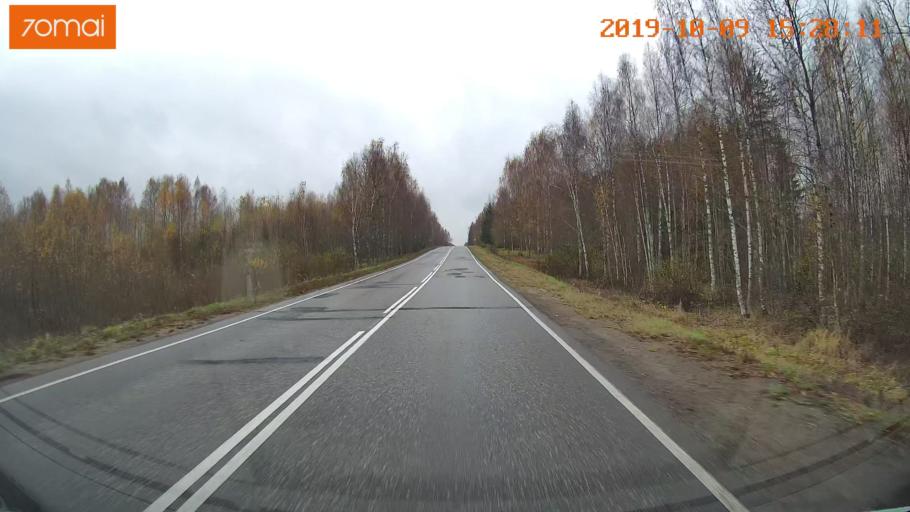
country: RU
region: Kostroma
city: Susanino
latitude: 58.0060
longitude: 41.3643
